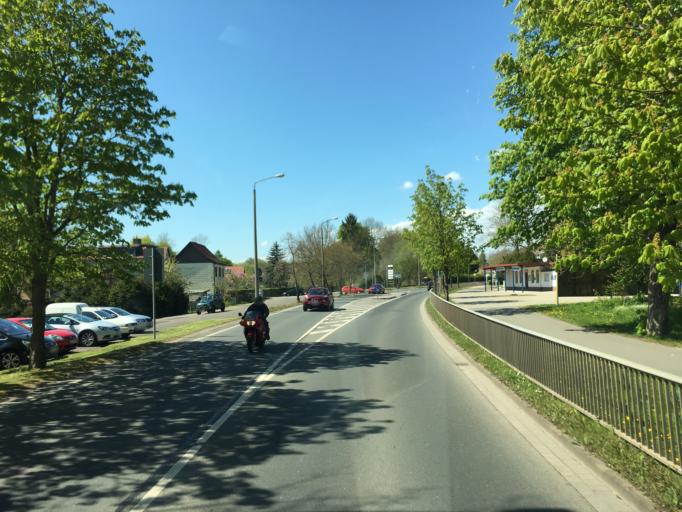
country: DE
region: Thuringia
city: Nordhausen
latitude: 51.5198
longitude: 10.7821
